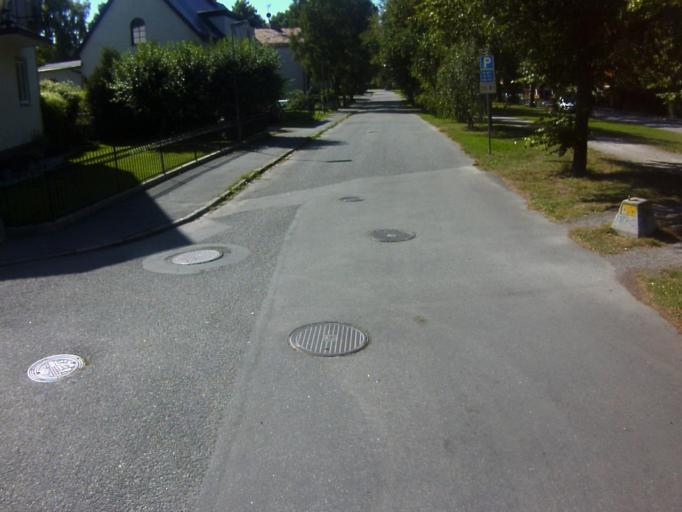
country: SE
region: Soedermanland
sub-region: Eskilstuna Kommun
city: Eskilstuna
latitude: 59.3697
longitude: 16.5279
